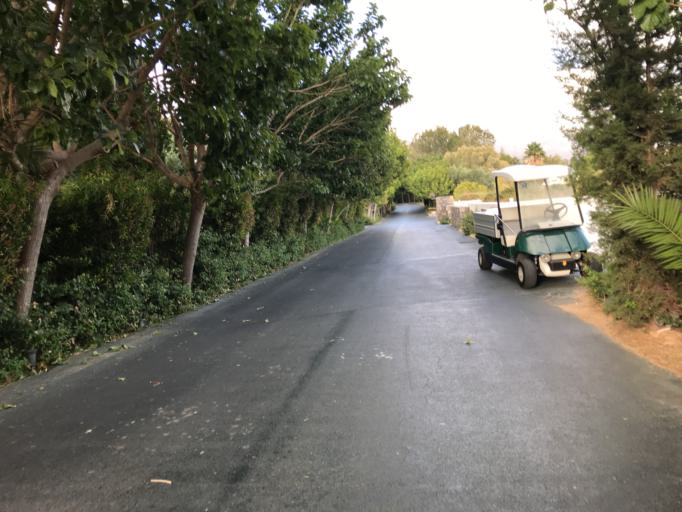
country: GR
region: Attica
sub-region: Nomarchia Anatolikis Attikis
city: Saronida
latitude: 37.7773
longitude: 23.8881
